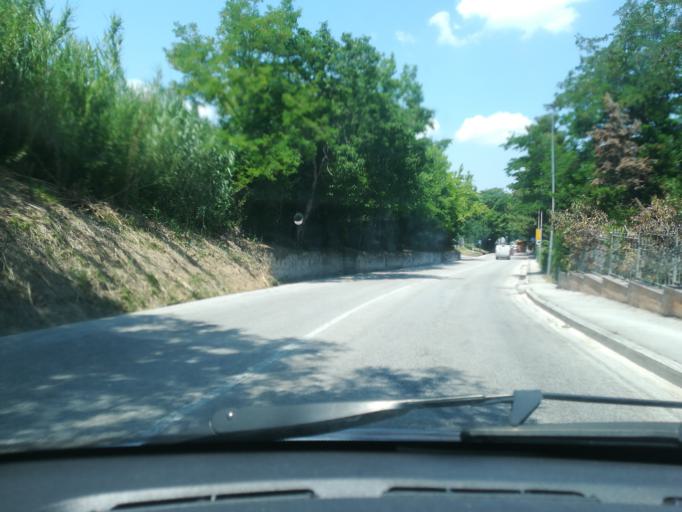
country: IT
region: The Marches
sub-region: Provincia di Macerata
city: Villa Potenza
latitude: 43.3100
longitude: 13.4361
